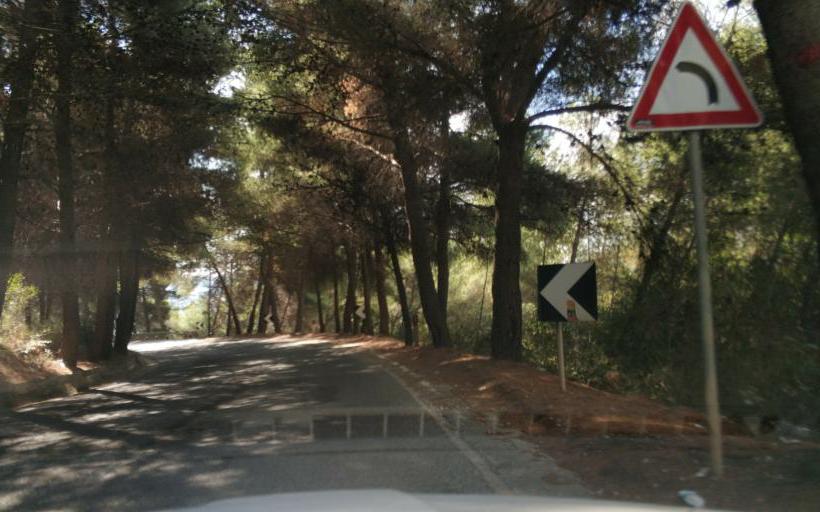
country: AL
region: Durres
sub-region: Rrethi i Krujes
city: Kruje
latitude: 41.4905
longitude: 19.7667
